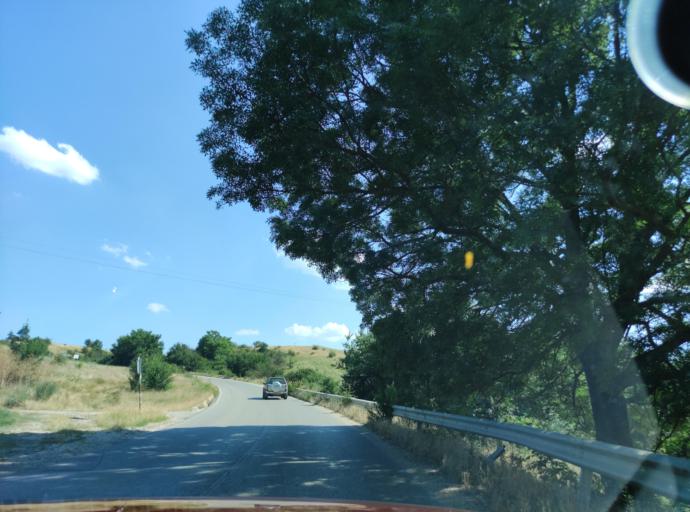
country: BG
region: Pleven
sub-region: Obshtina Cherven Bryag
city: Koynare
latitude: 43.3748
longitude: 24.0587
